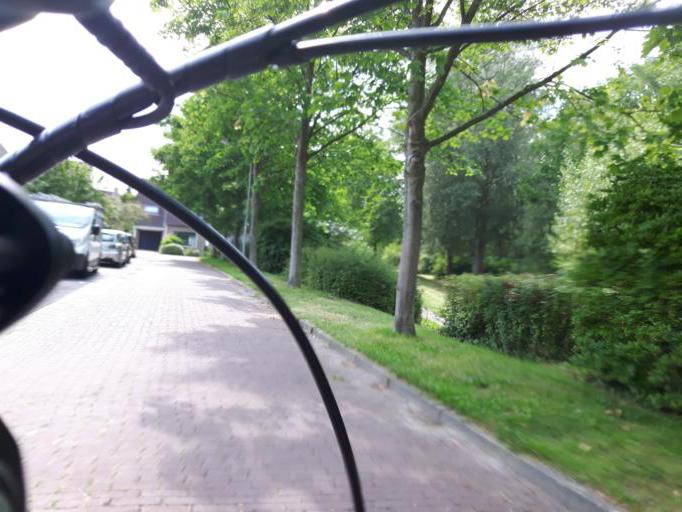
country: NL
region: Zeeland
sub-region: Gemeente Goes
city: Goes
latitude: 51.5163
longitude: 3.9057
